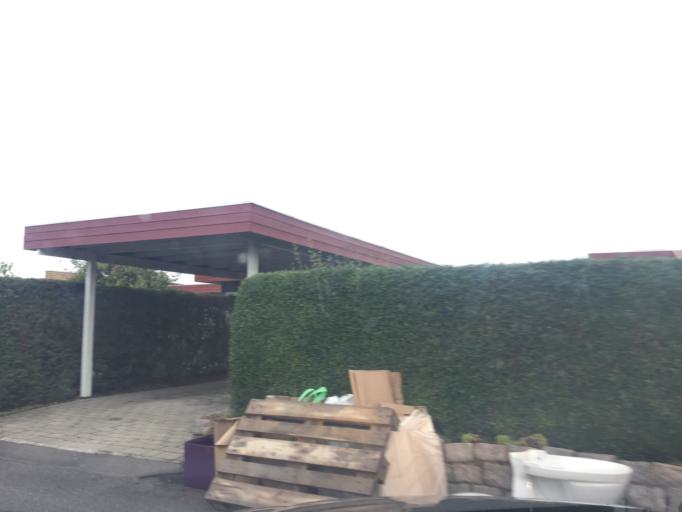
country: DK
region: Capital Region
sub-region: Albertslund Kommune
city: Albertslund
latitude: 55.6484
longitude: 12.3652
